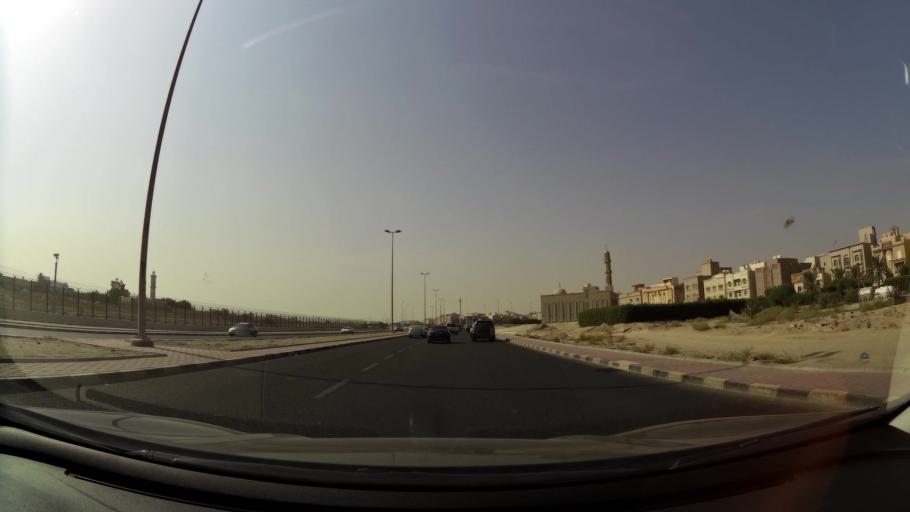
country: KW
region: Al Ahmadi
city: Al Mahbulah
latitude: 29.1199
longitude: 48.1142
